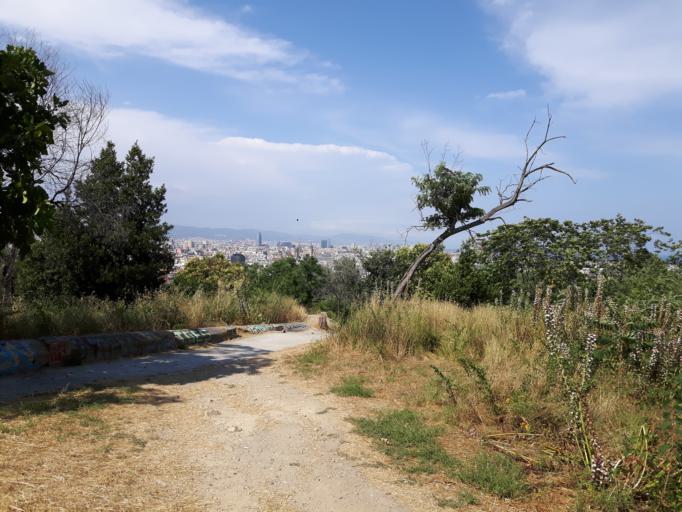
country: ES
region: Catalonia
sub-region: Provincia de Barcelona
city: Sants-Montjuic
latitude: 41.3695
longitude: 2.1628
